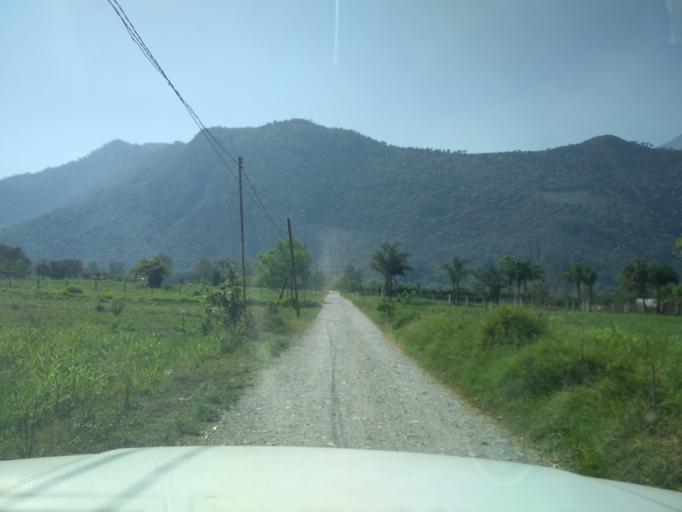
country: MX
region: Veracruz
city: Jalapilla
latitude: 18.8139
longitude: -97.0868
